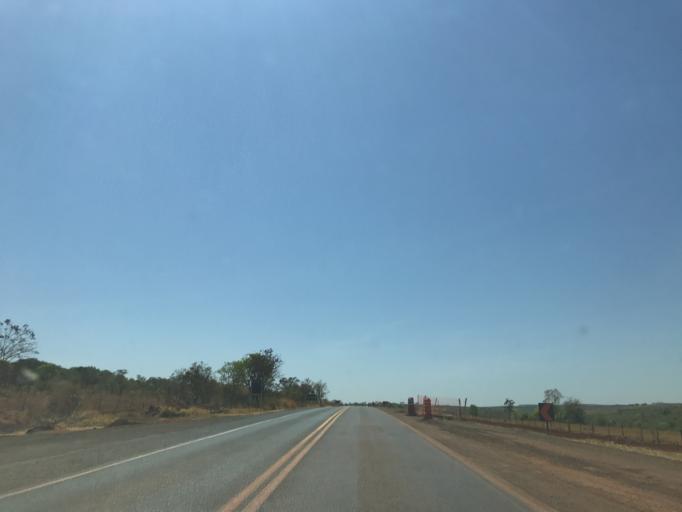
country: BR
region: Minas Gerais
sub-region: Prata
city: Prata
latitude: -19.4324
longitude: -48.8890
